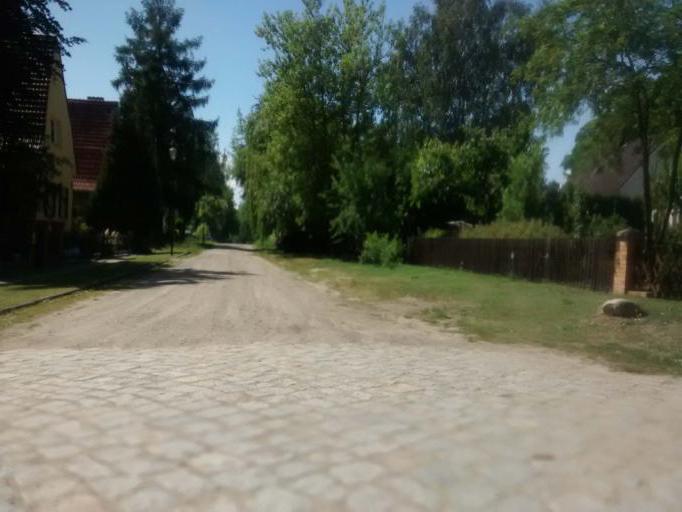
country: DE
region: Brandenburg
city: Hohen Neuendorf
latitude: 52.6771
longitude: 13.2725
